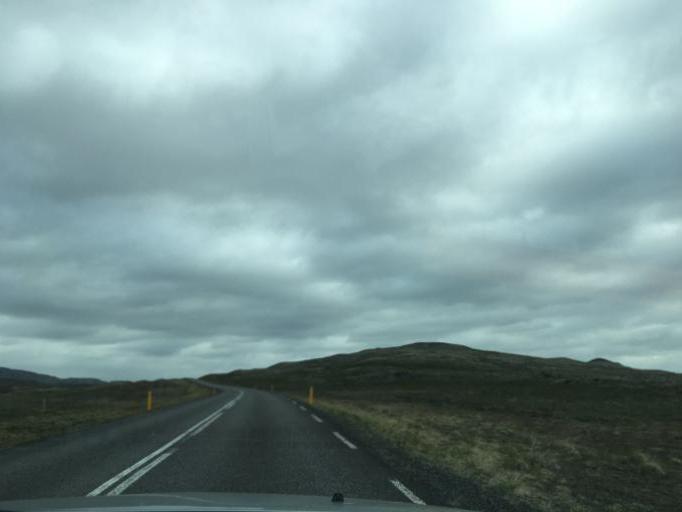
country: IS
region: South
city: Vestmannaeyjar
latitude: 64.2659
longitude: -20.1938
